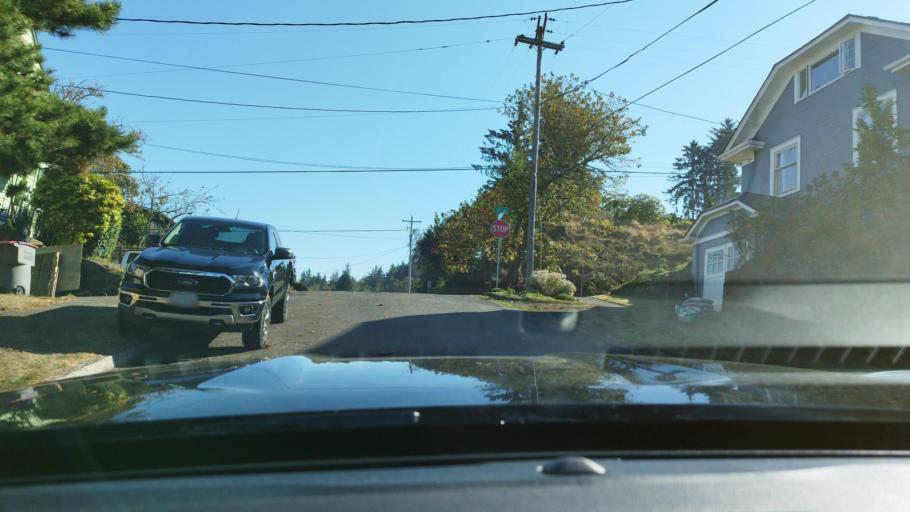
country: US
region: Oregon
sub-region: Clatsop County
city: Astoria
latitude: 46.1831
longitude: -123.8272
